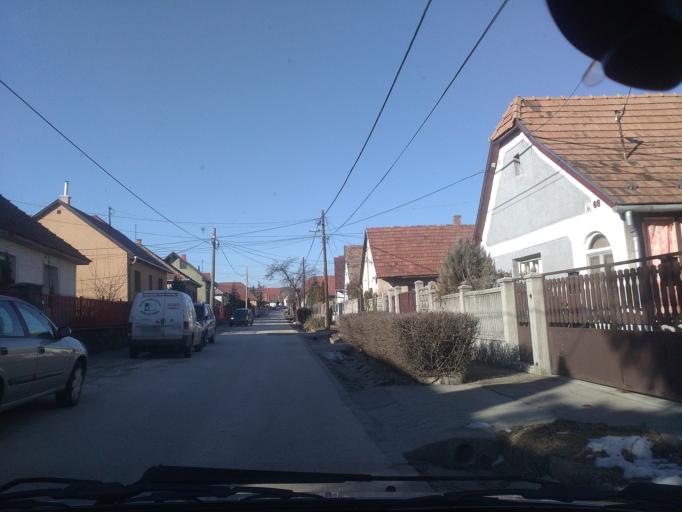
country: HU
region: Pest
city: Pilisvorosvar
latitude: 47.6162
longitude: 18.9098
